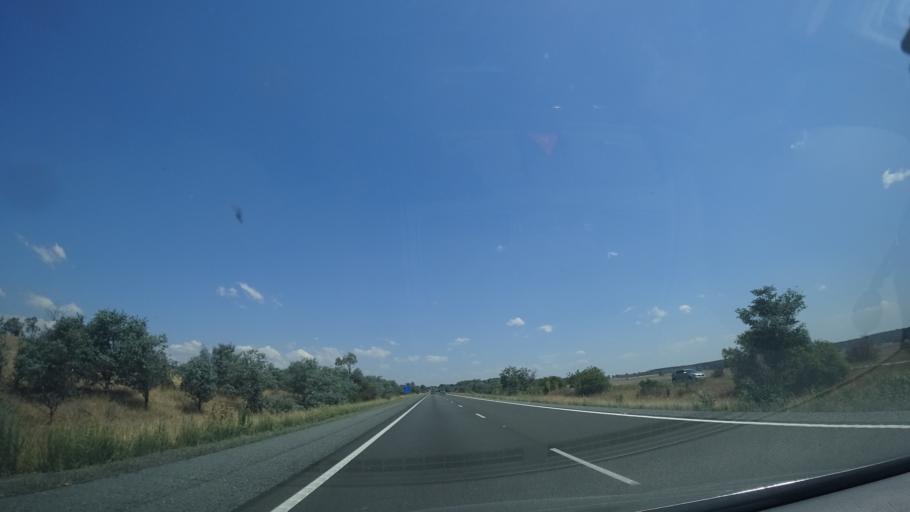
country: AU
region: New South Wales
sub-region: Wingecarribee
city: Moss Vale
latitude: -34.5394
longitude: 150.2788
